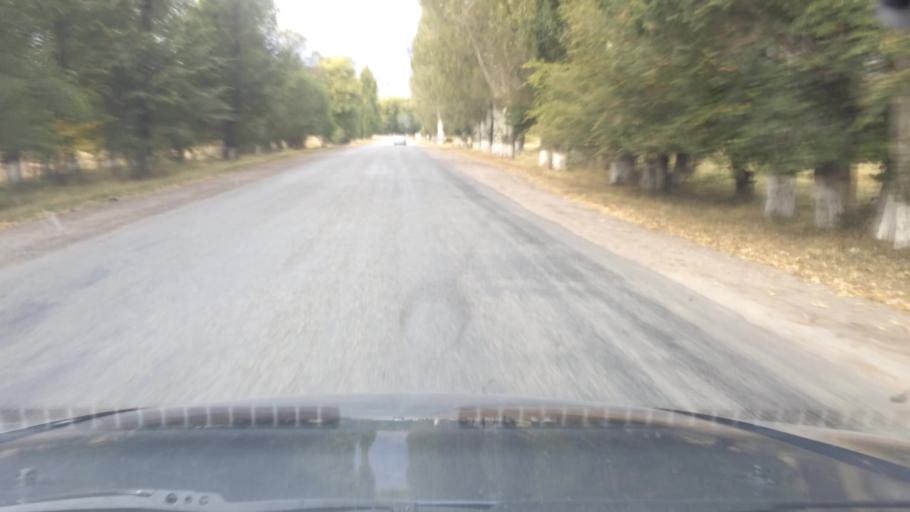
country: KG
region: Ysyk-Koel
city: Tyup
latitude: 42.7860
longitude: 78.2678
